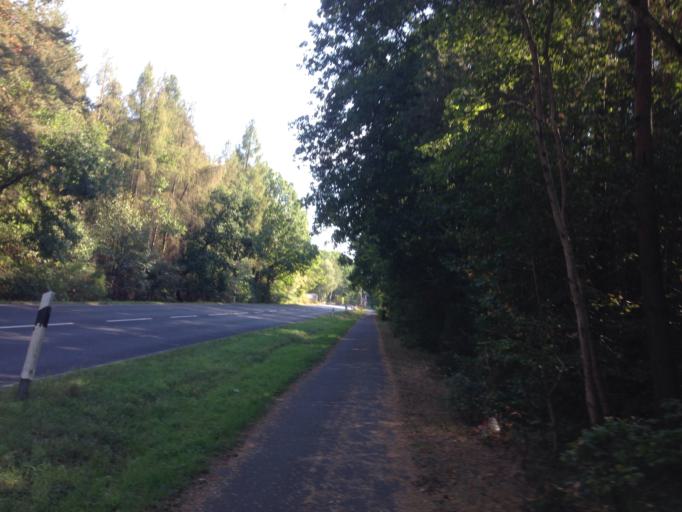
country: DE
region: Hesse
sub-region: Regierungsbezirk Giessen
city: Giessen
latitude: 50.5572
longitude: 8.6961
